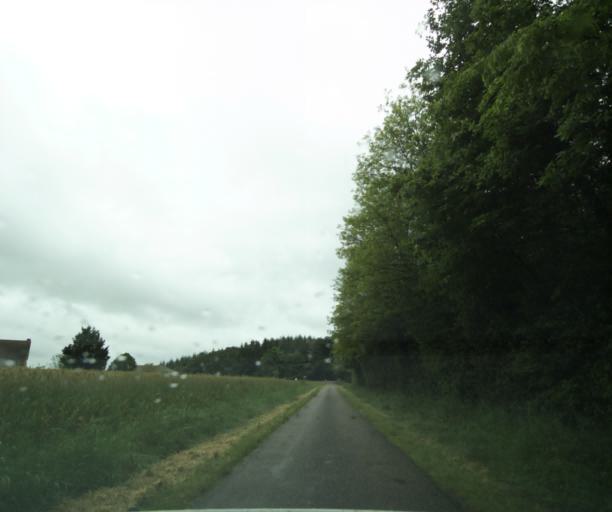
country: FR
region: Bourgogne
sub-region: Departement de Saone-et-Loire
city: Charolles
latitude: 46.4774
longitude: 4.4139
